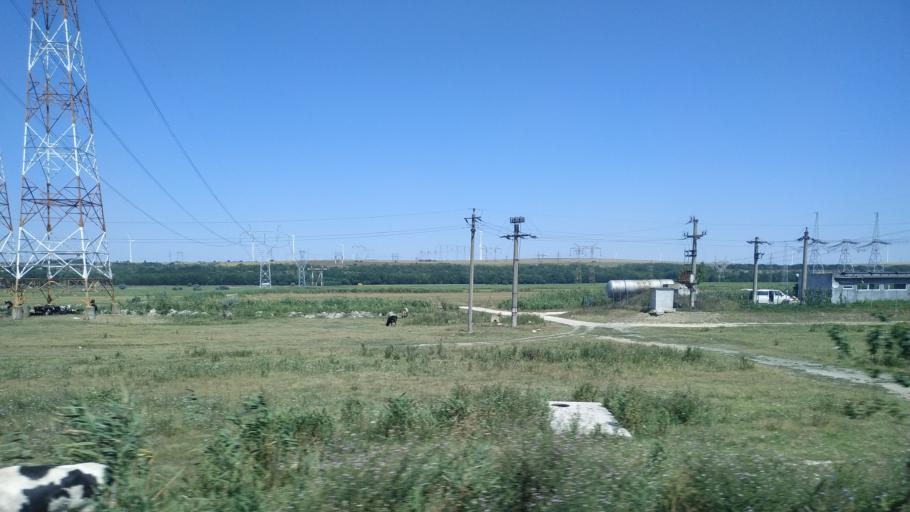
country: RO
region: Constanta
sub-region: Comuna Saligny
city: Faclia
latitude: 44.2699
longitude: 28.1204
